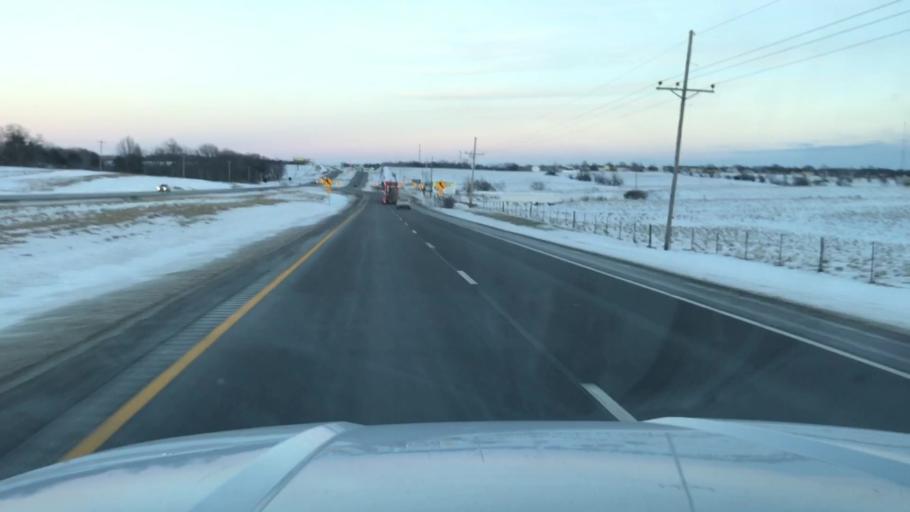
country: US
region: Missouri
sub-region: Clinton County
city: Cameron
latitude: 39.7539
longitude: -94.2712
